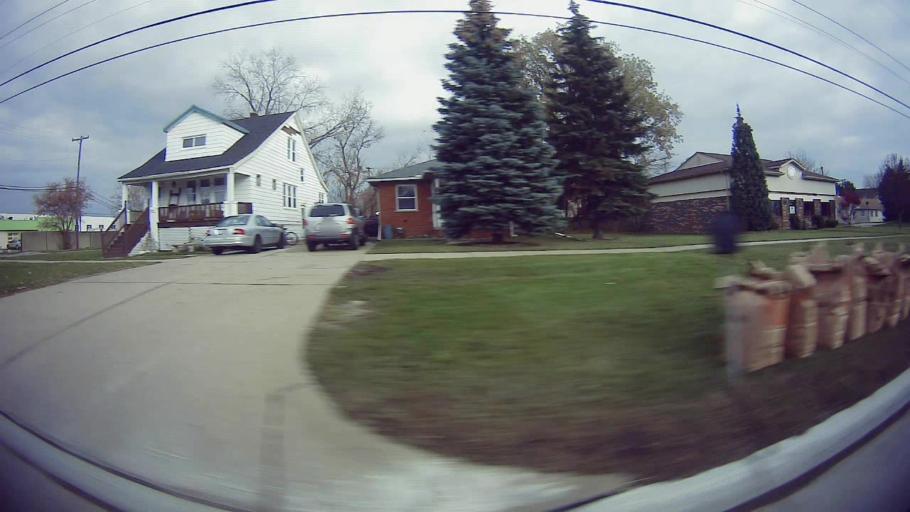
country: US
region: Michigan
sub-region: Macomb County
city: Eastpointe
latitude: 42.4908
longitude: -82.9870
